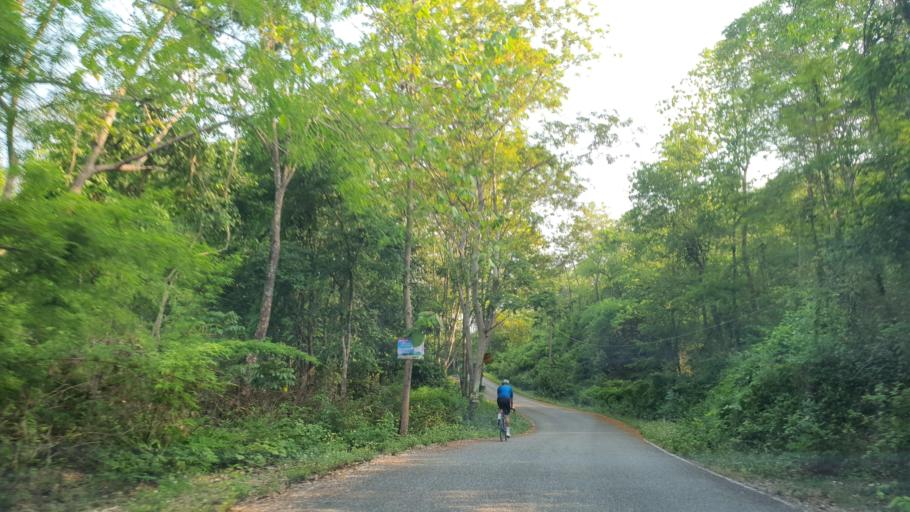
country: TH
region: Chiang Mai
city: Mae Wang
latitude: 18.6844
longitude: 98.8065
